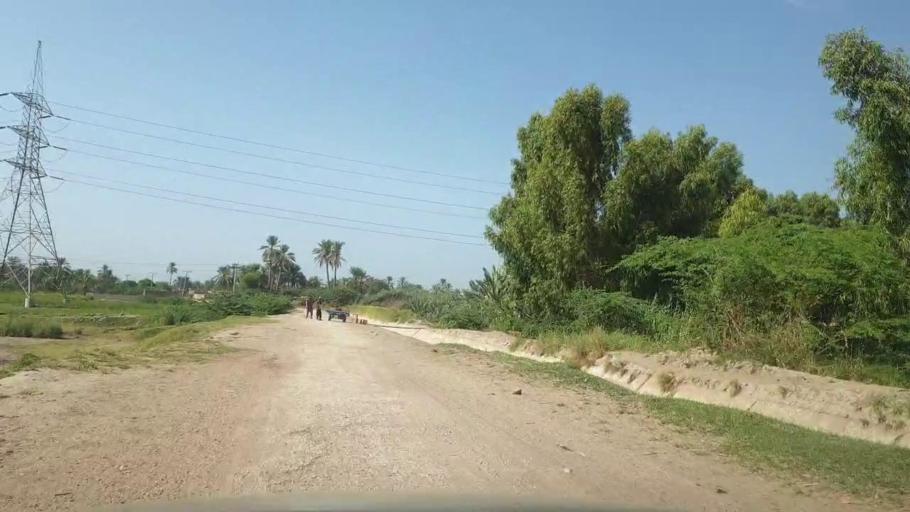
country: PK
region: Sindh
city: Rohri
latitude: 27.6625
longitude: 68.8839
